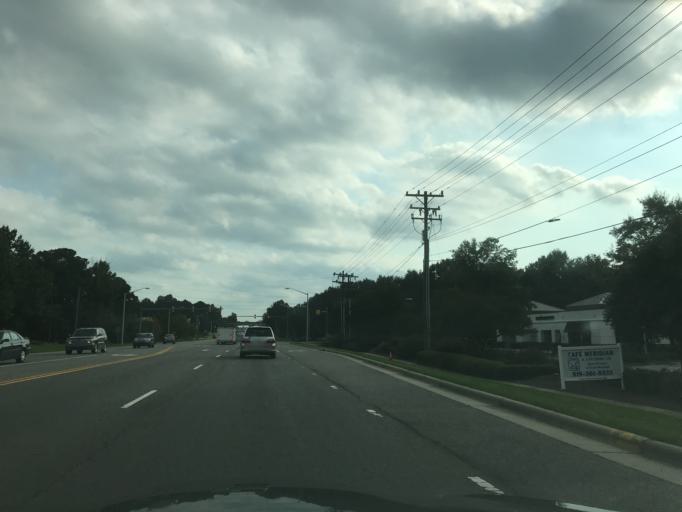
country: US
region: North Carolina
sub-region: Durham County
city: Durham
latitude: 35.9120
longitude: -78.8927
